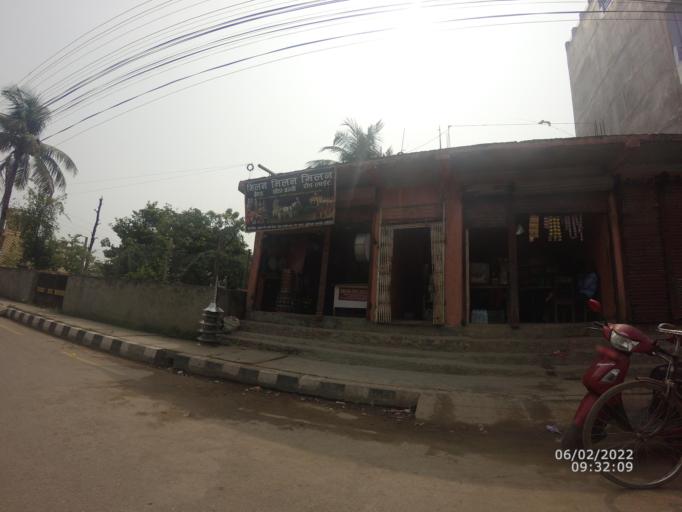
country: NP
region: Western Region
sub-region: Lumbini Zone
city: Bhairahawa
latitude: 27.4985
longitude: 83.4506
